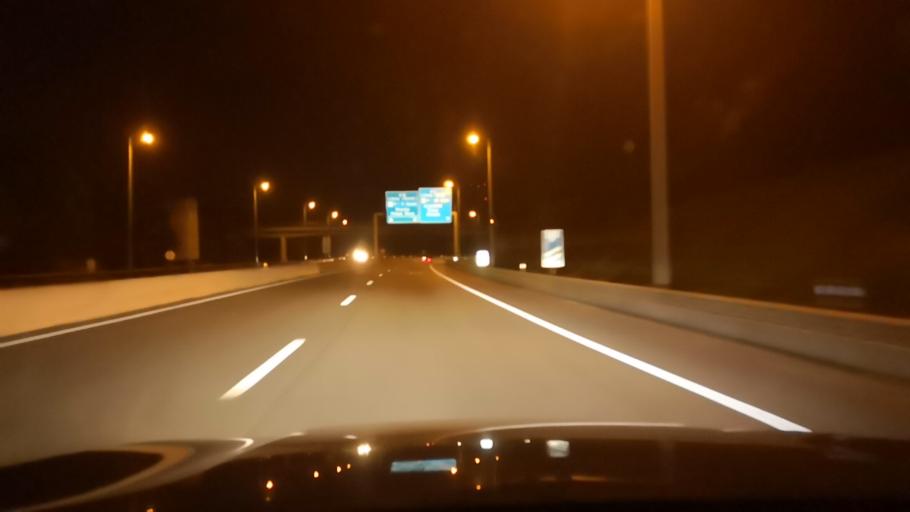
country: PT
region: Setubal
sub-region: Palmela
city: Palmela
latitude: 38.5726
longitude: -8.8665
